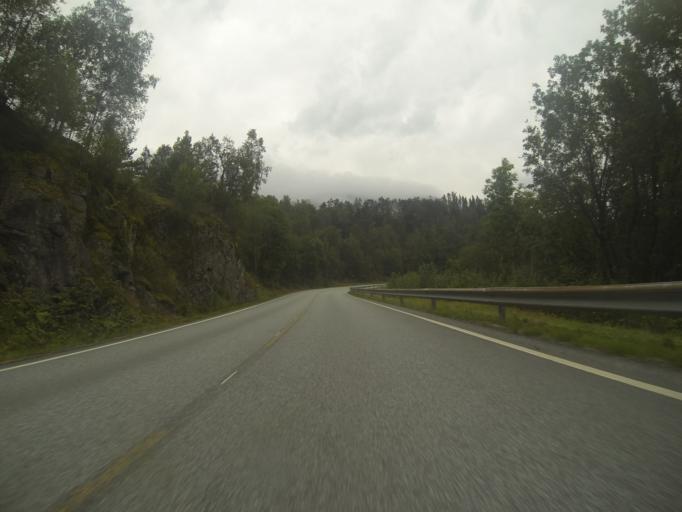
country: NO
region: Rogaland
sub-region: Suldal
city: Sand
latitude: 59.5654
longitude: 6.2737
